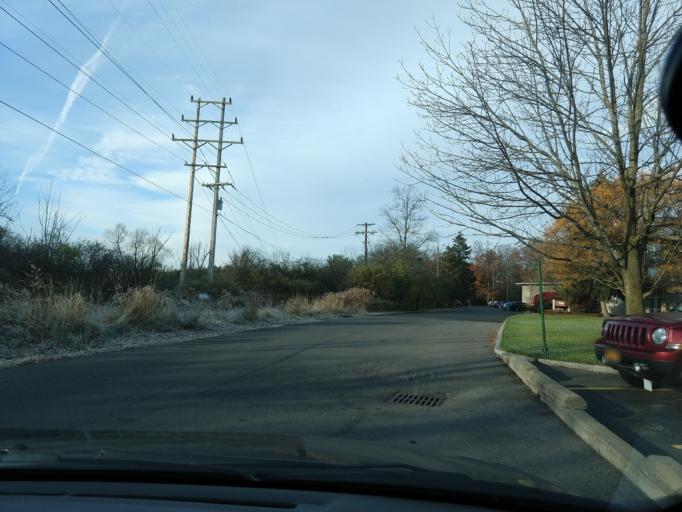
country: US
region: New York
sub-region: Tompkins County
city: Lansing
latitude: 42.4781
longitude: -76.4857
